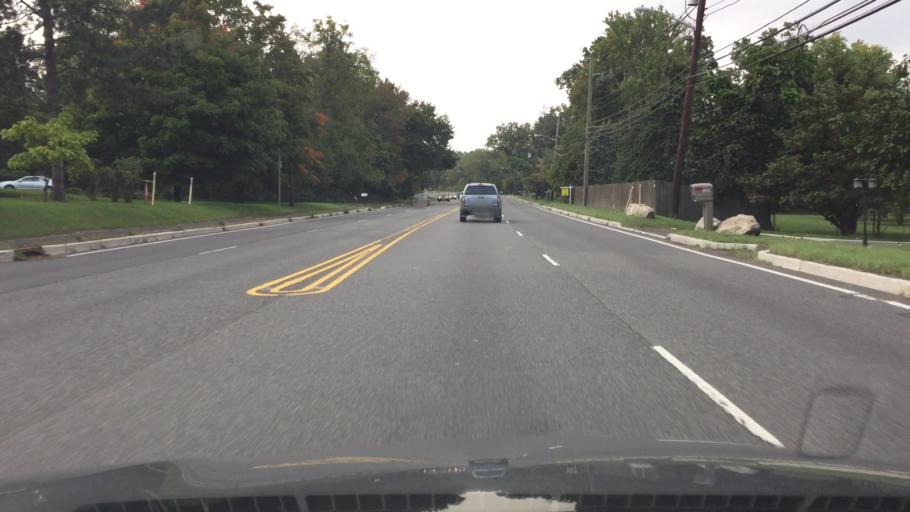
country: US
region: New Jersey
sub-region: Somerset County
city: Somerset
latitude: 40.5300
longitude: -74.4997
